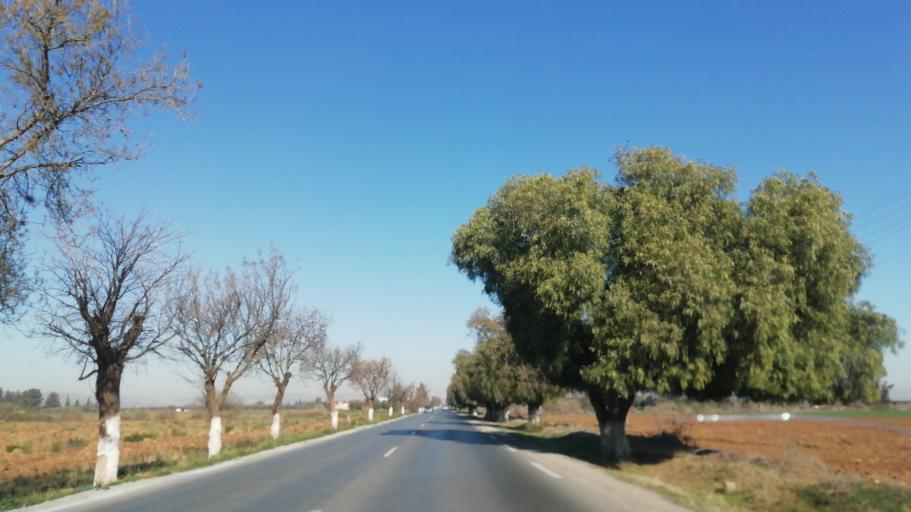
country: DZ
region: Mascara
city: Mascara
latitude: 35.2881
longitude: 0.1278
